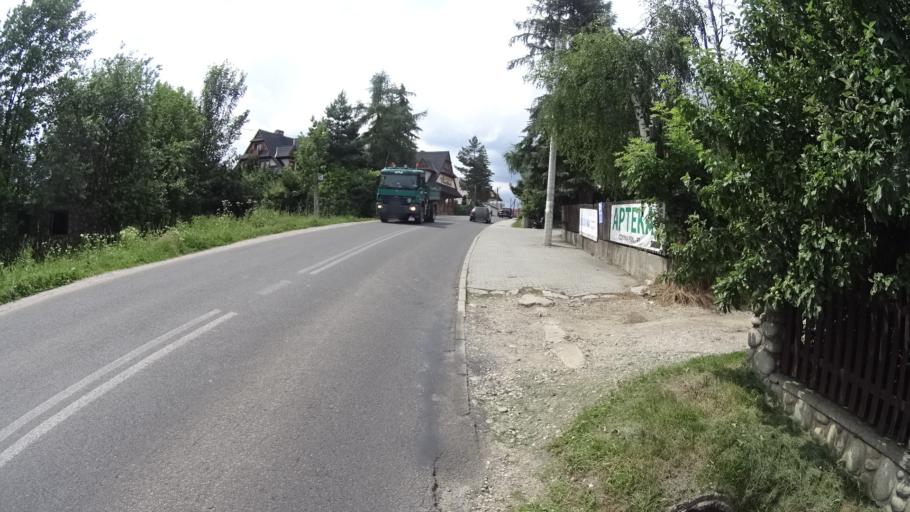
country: PL
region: Lesser Poland Voivodeship
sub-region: Powiat tatrzanski
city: Zakopane
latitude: 49.3383
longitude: 19.9502
